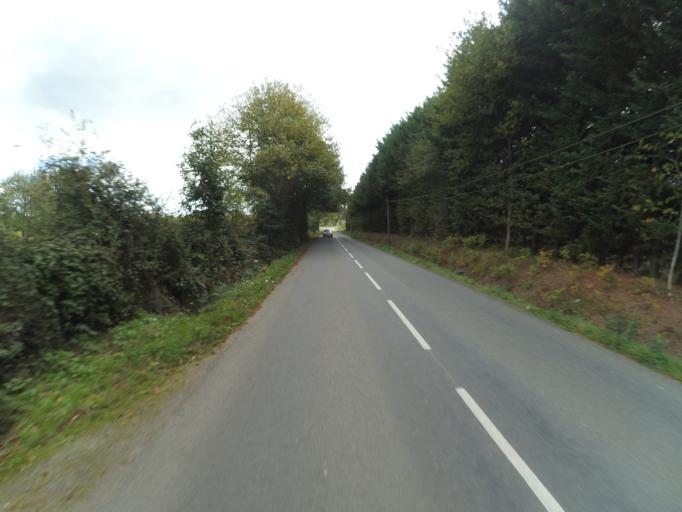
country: FR
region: Pays de la Loire
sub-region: Departement de la Loire-Atlantique
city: Casson
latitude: 47.3636
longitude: -1.5453
